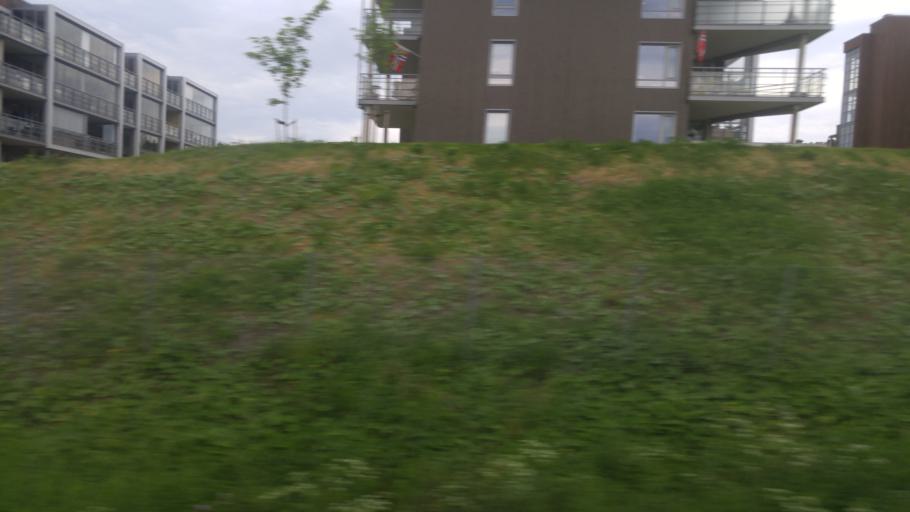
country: NO
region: Sor-Trondelag
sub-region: Trondheim
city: Trondheim
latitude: 63.4313
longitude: 10.5076
